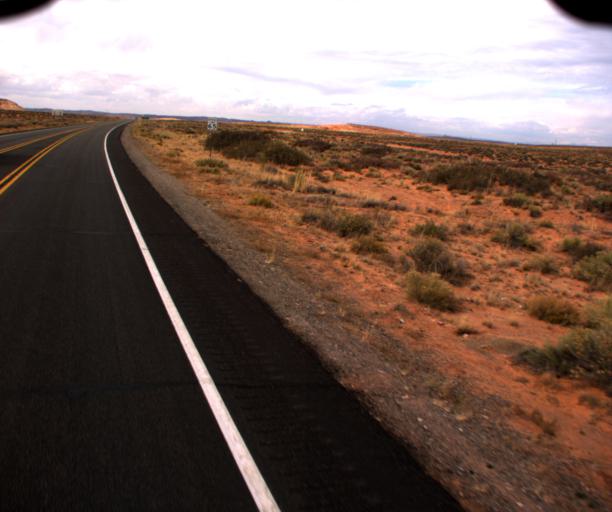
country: US
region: Arizona
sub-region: Apache County
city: Many Farms
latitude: 36.9256
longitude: -109.6155
